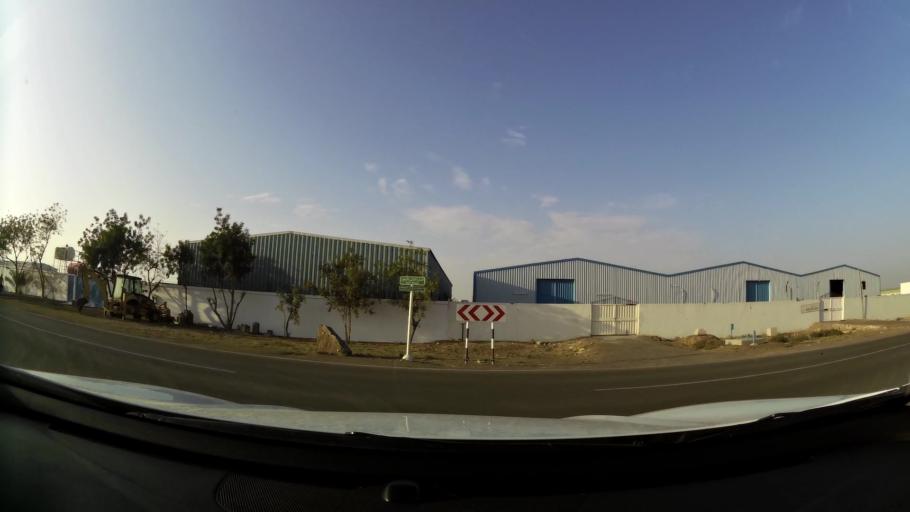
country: AE
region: Abu Dhabi
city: Al Ain
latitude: 24.1487
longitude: 55.8416
